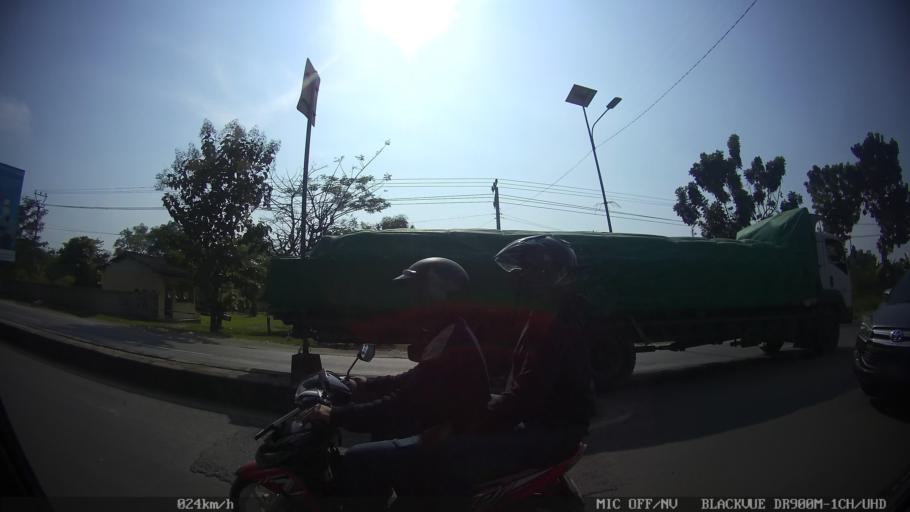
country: ID
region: Lampung
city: Natar
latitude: -5.3019
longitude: 105.1919
